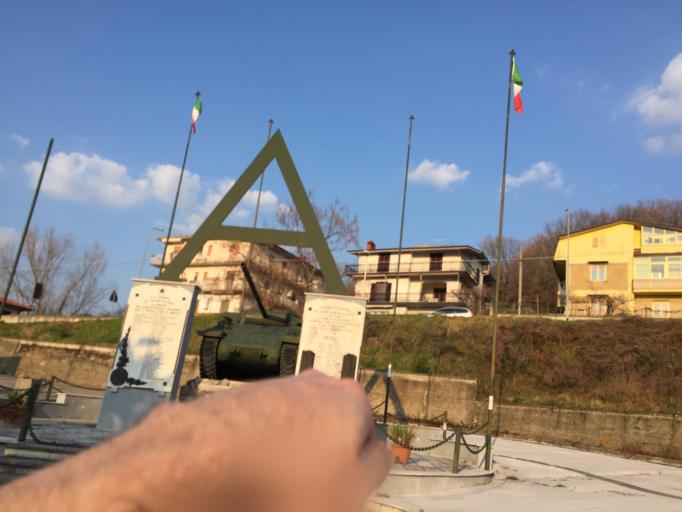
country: IT
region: Campania
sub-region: Provincia di Benevento
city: Arpaise
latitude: 41.0320
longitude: 14.7448
